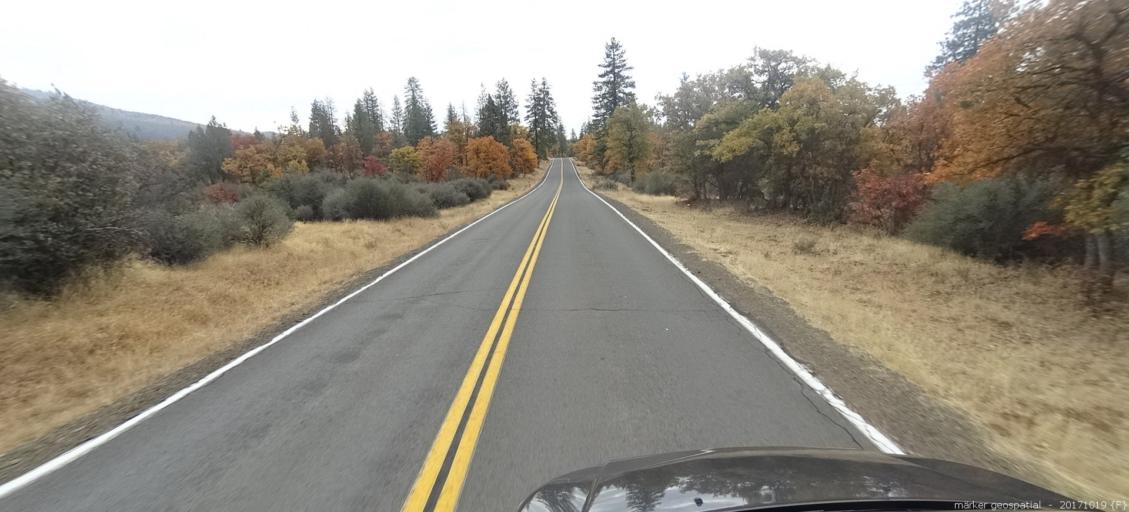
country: US
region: California
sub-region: Shasta County
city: Burney
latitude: 41.1484
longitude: -121.3513
